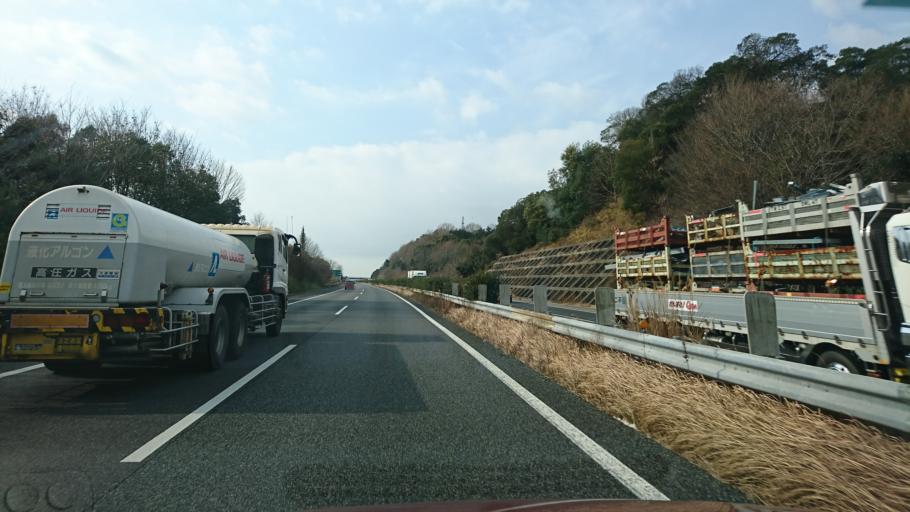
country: JP
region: Okayama
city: Kurashiki
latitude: 34.5785
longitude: 133.6755
